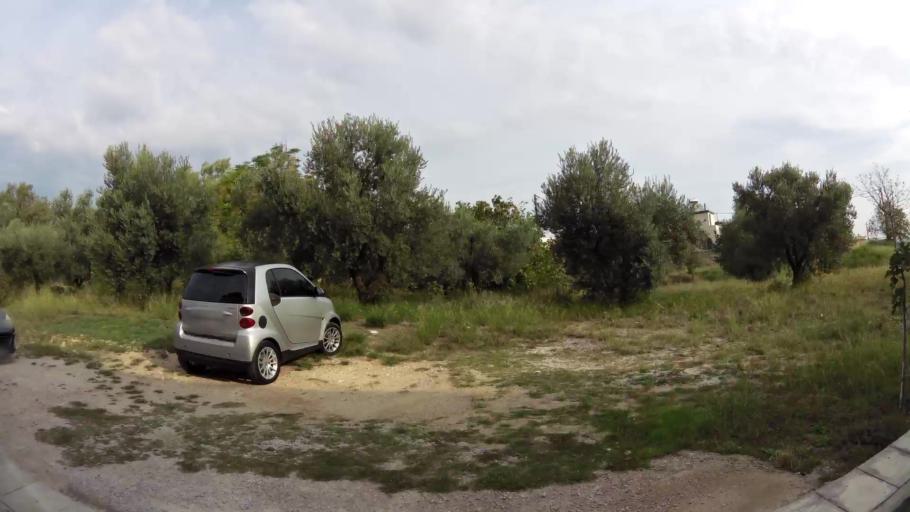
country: GR
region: Attica
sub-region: Nomarchia Athinas
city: Kamateron
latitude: 38.0547
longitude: 23.7036
